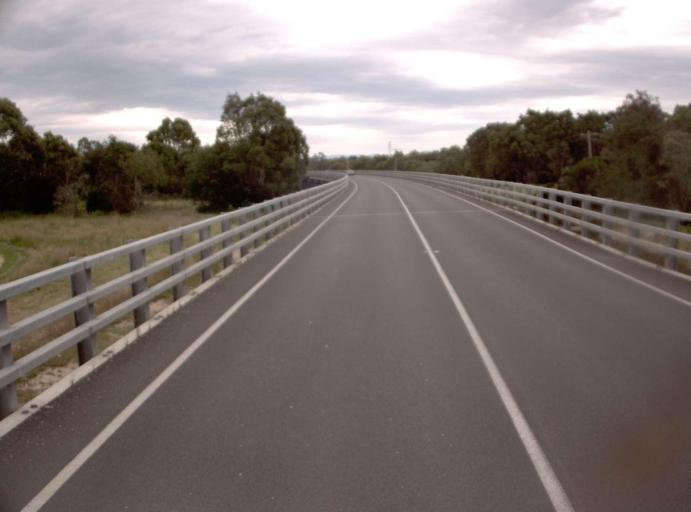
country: AU
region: Victoria
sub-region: Wellington
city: Sale
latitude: -38.1275
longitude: 147.0703
